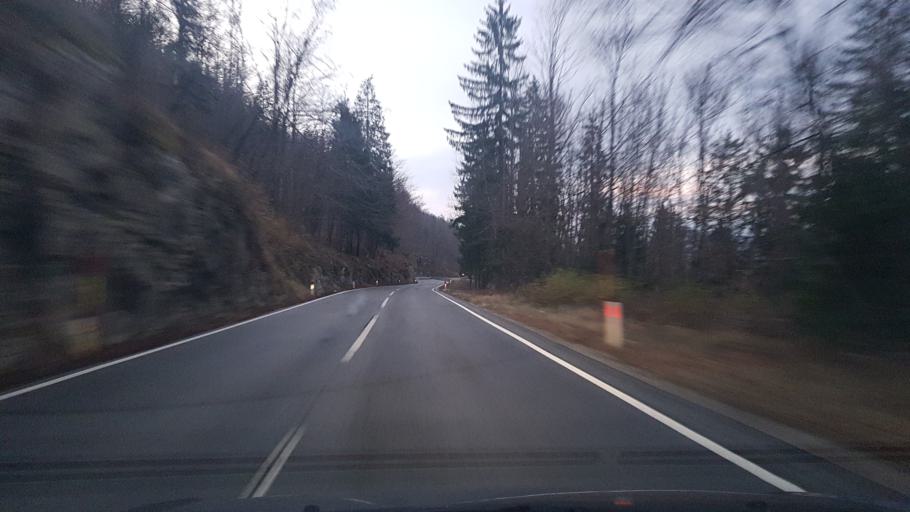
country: SI
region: Idrija
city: Idrija
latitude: 45.9533
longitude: 14.0782
